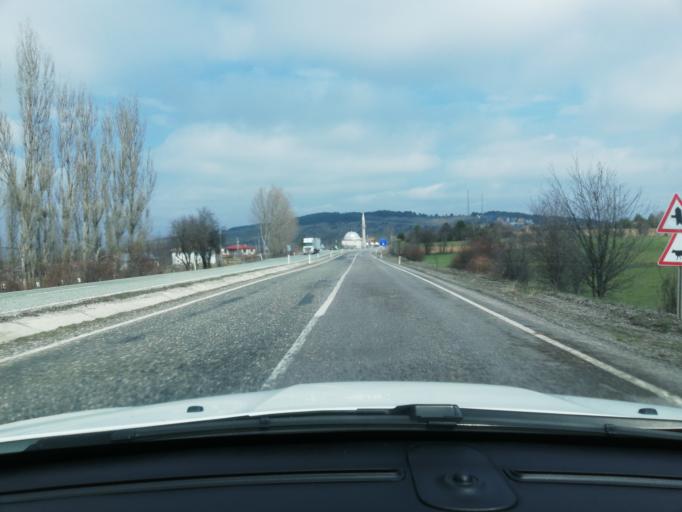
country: TR
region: Kastamonu
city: Kuzyaka
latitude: 41.2240
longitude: 33.7934
